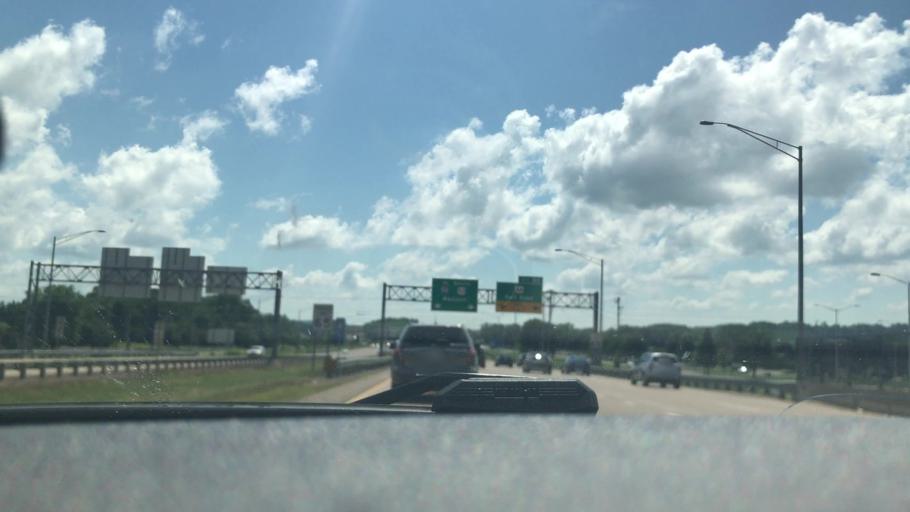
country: US
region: Wisconsin
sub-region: Eau Claire County
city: Altoona
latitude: 44.7838
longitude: -91.4476
